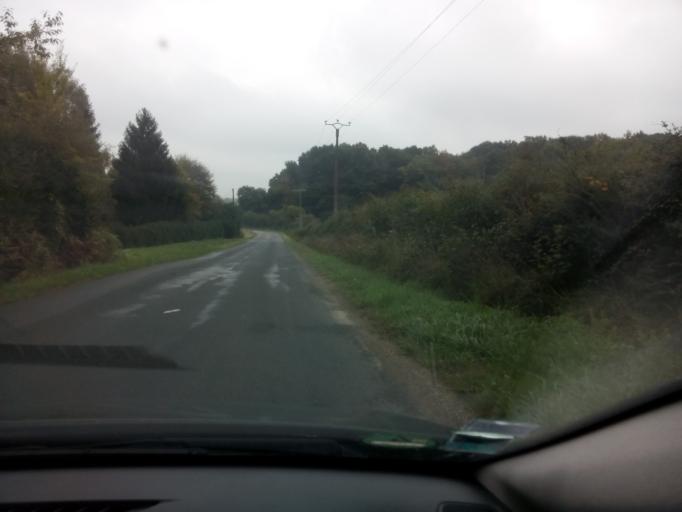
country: FR
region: Pays de la Loire
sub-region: Departement de Maine-et-Loire
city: Soulaire-et-Bourg
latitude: 47.6149
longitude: -0.5689
